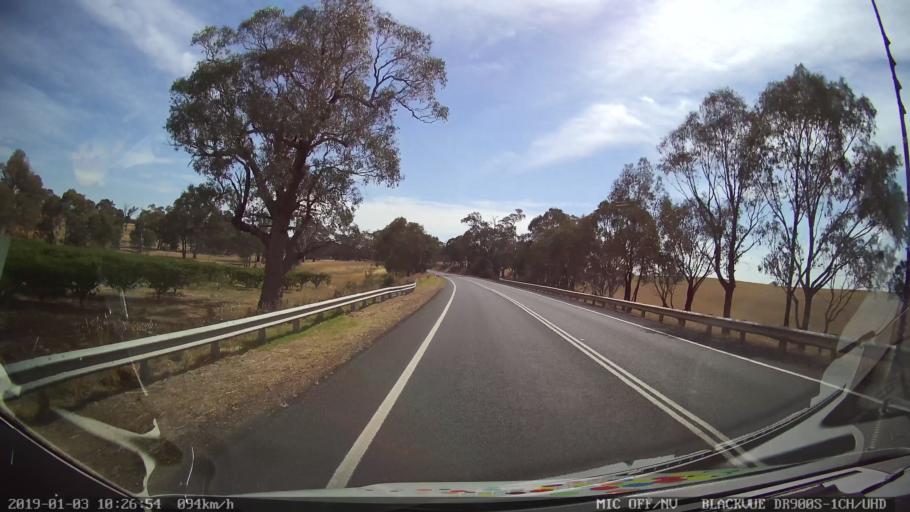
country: AU
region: New South Wales
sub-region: Young
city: Young
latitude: -34.4083
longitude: 148.2544
